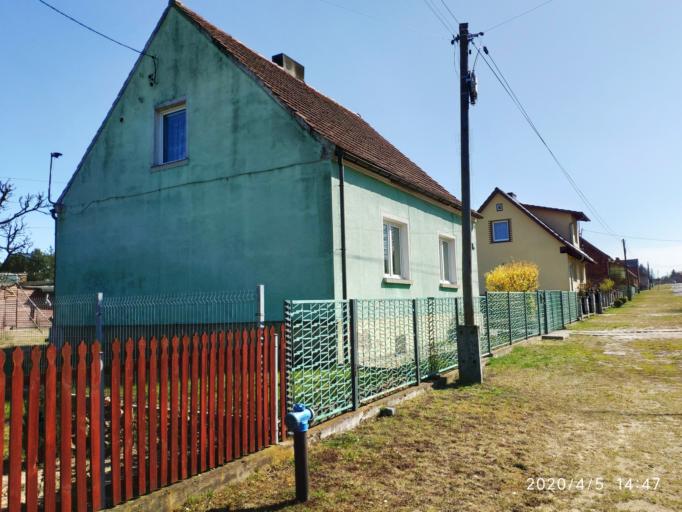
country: PL
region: Lubusz
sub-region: Powiat krosnienski
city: Dabie
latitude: 52.0321
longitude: 15.2494
